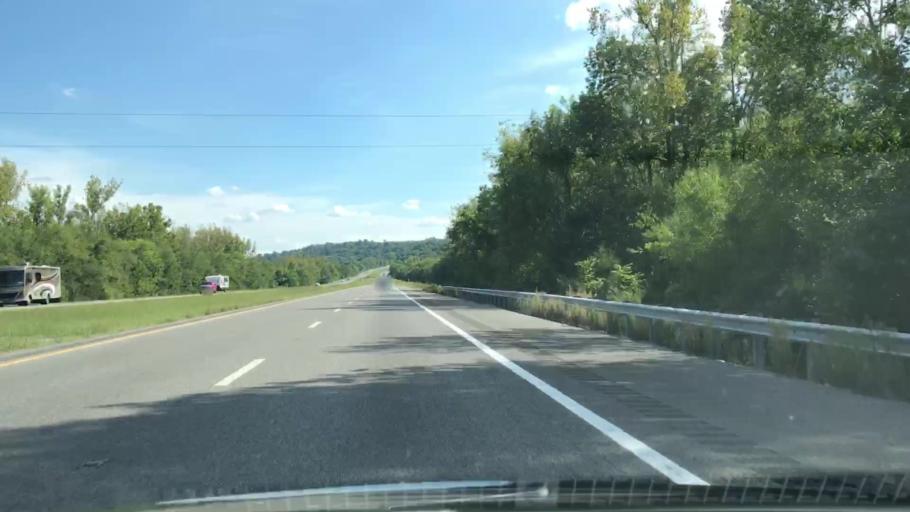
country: US
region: Alabama
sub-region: Limestone County
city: Ardmore
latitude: 35.1379
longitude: -86.8783
